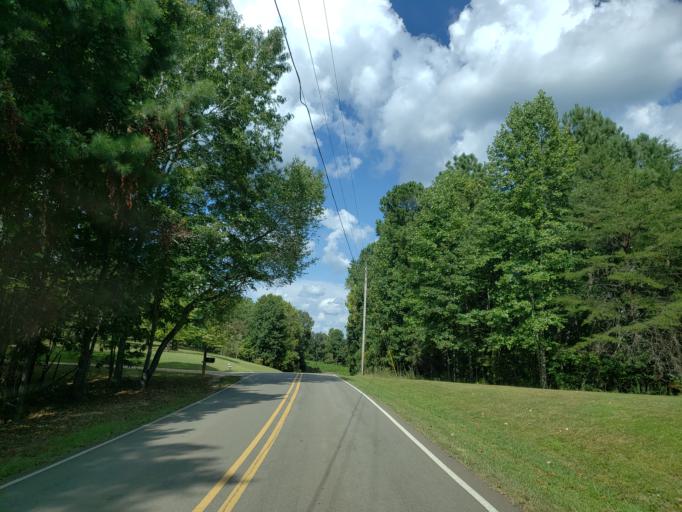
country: US
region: Georgia
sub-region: Pickens County
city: Jasper
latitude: 34.4215
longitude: -84.4436
